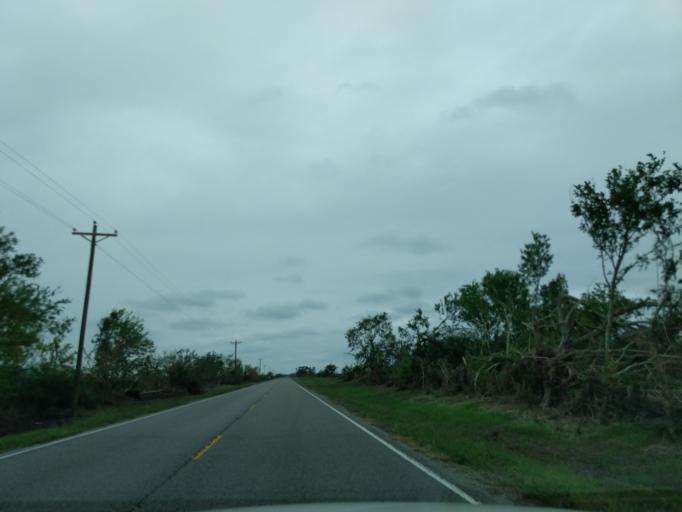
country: US
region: Louisiana
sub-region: Cameron Parish
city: Cameron
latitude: 29.7868
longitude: -93.1560
